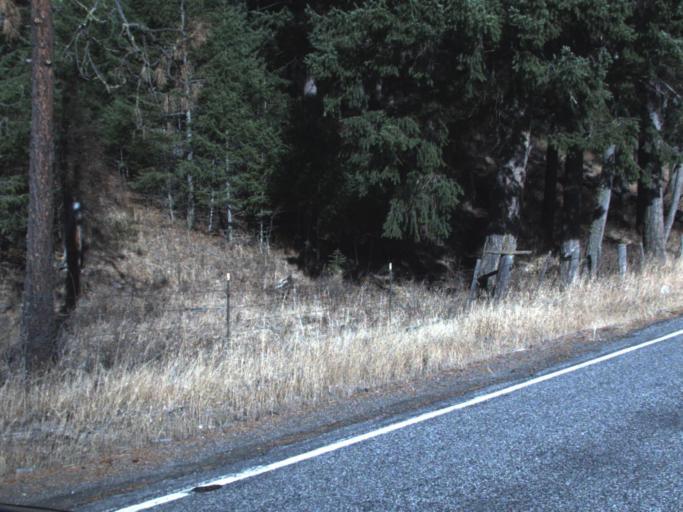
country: US
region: Washington
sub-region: Ferry County
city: Republic
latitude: 48.5795
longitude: -118.7428
